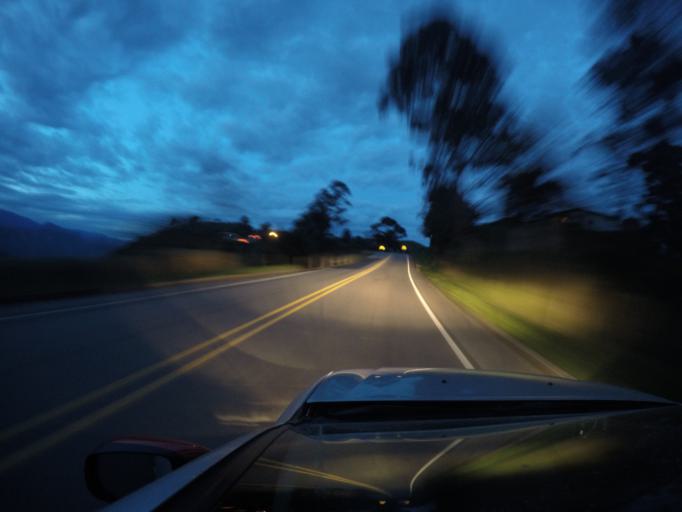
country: CO
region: Tolima
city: Fresno
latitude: 5.1558
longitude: -75.1001
